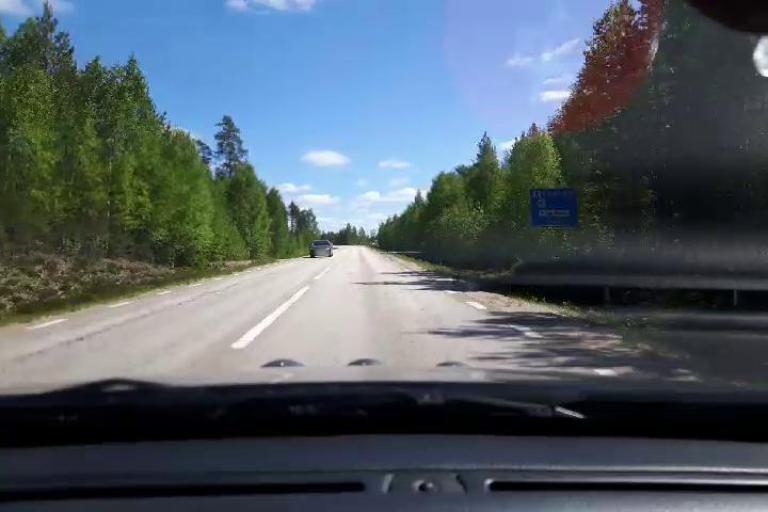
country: SE
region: Gaevleborg
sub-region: Ljusdals Kommun
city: Farila
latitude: 61.9884
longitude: 15.2784
